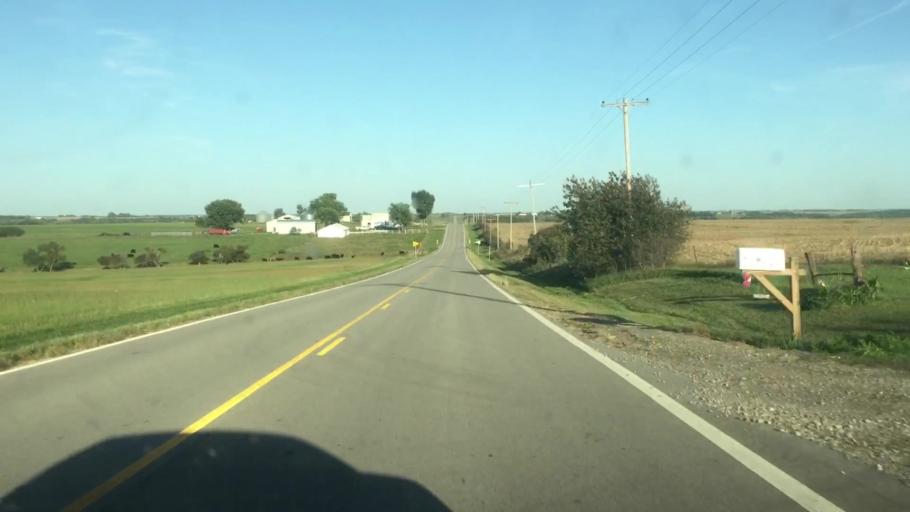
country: US
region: Kansas
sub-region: Brown County
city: Horton
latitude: 39.5876
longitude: -95.5823
